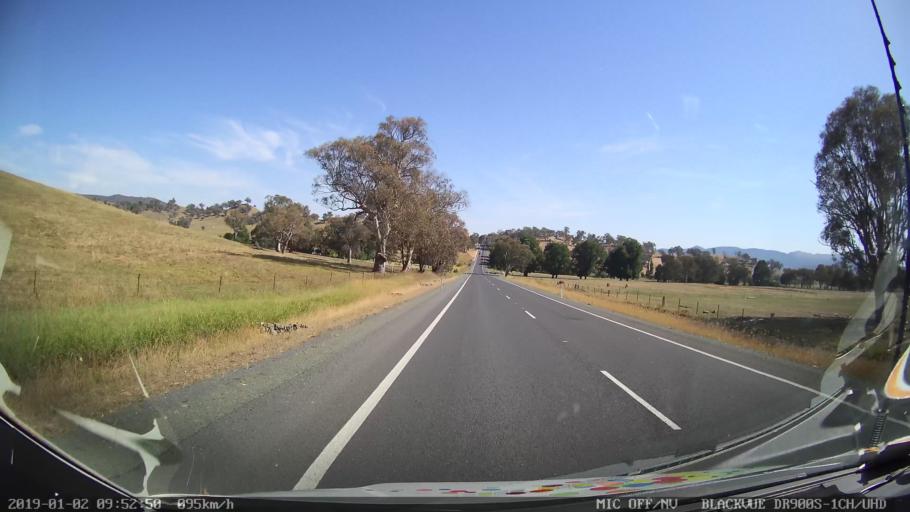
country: AU
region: New South Wales
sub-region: Tumut Shire
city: Tumut
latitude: -35.2560
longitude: 148.2041
